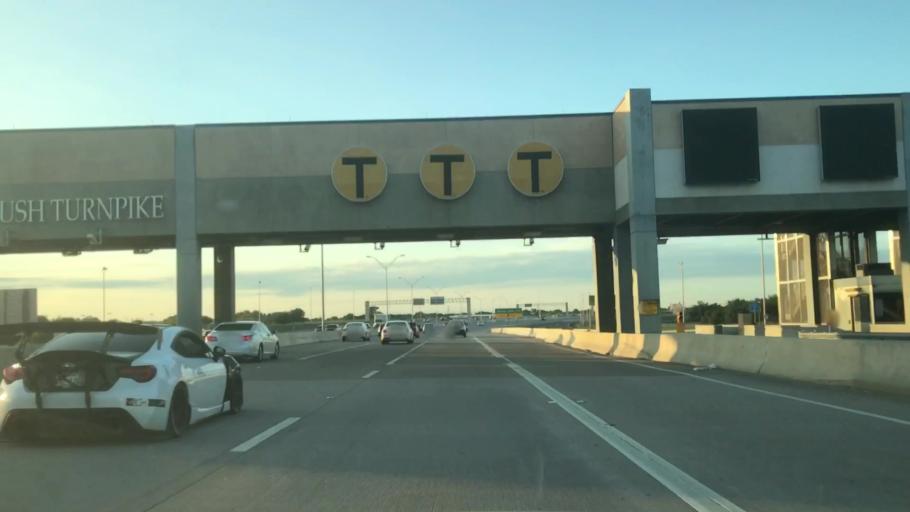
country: US
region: Texas
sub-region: Dallas County
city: Carrollton
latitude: 32.9589
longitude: -96.9292
